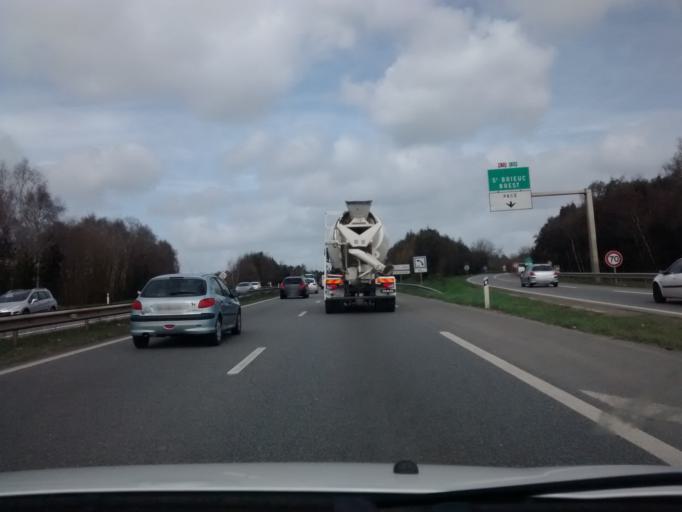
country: FR
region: Brittany
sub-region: Departement d'Ille-et-Vilaine
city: Vezin-le-Coquet
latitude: 48.1172
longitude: -1.7195
